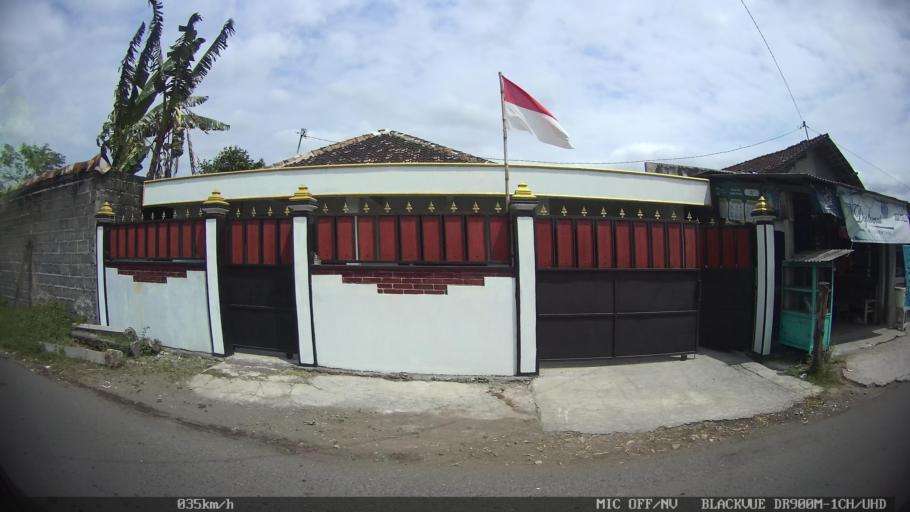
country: ID
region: Daerah Istimewa Yogyakarta
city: Depok
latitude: -7.7945
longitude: 110.4580
